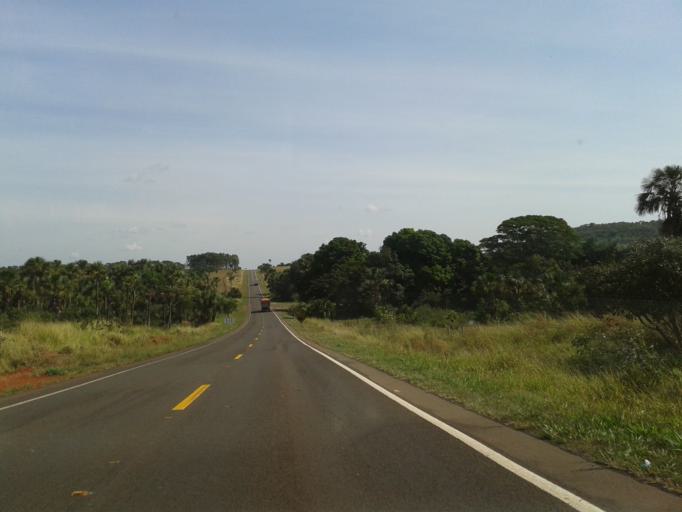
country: BR
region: Minas Gerais
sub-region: Campina Verde
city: Campina Verde
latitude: -19.5223
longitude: -49.5659
